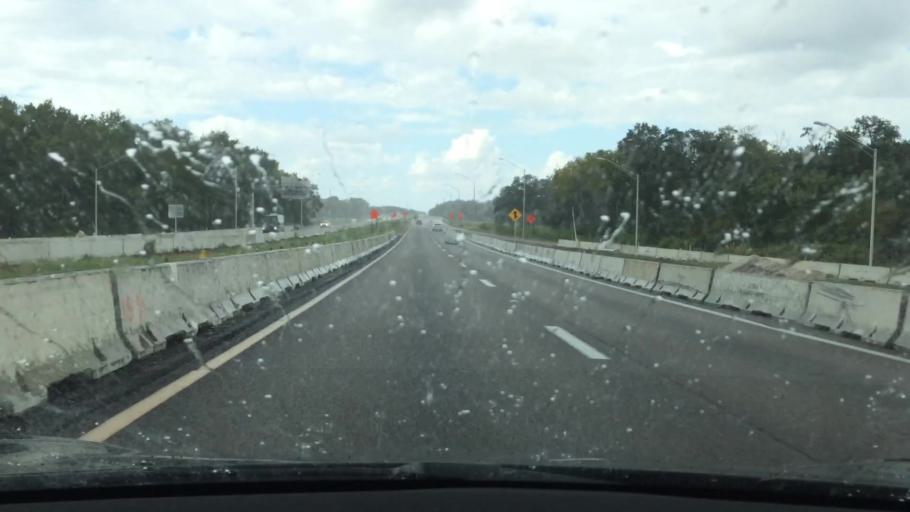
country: US
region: Florida
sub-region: Orange County
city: Wedgefield
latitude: 28.4517
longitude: -81.0978
